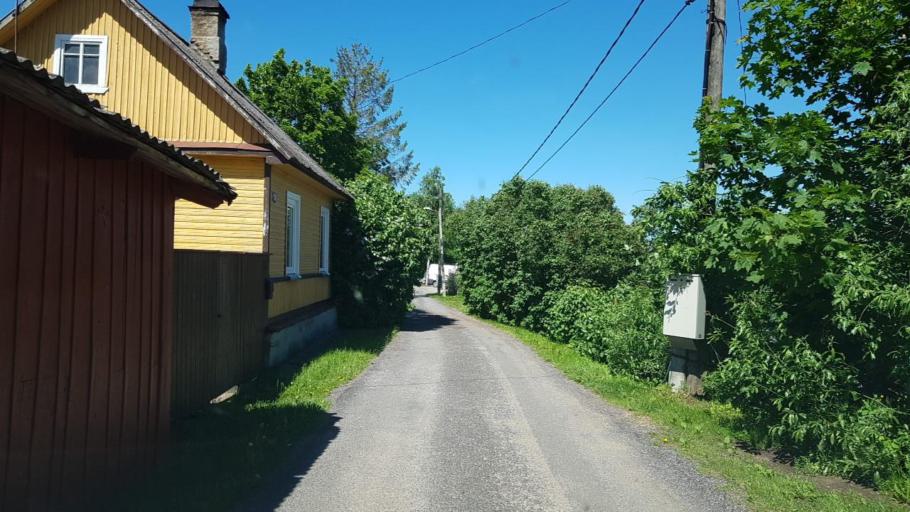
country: EE
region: Ida-Virumaa
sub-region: Narva linn
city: Narva
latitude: 59.3905
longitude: 28.1990
